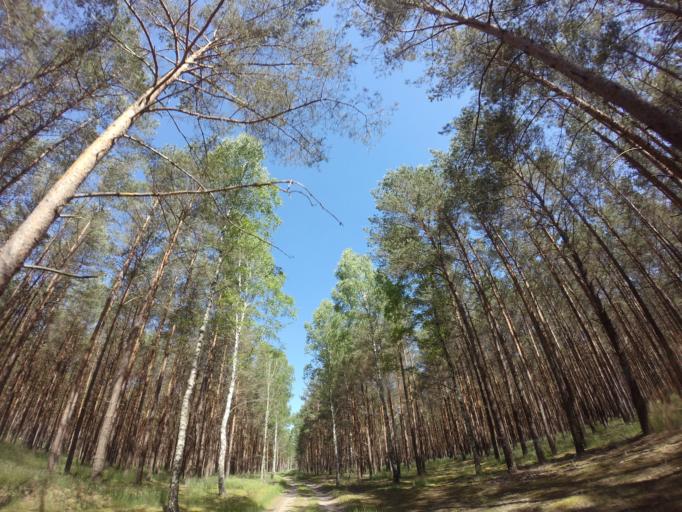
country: PL
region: West Pomeranian Voivodeship
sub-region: Powiat drawski
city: Kalisz Pomorski
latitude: 53.1814
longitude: 15.9828
